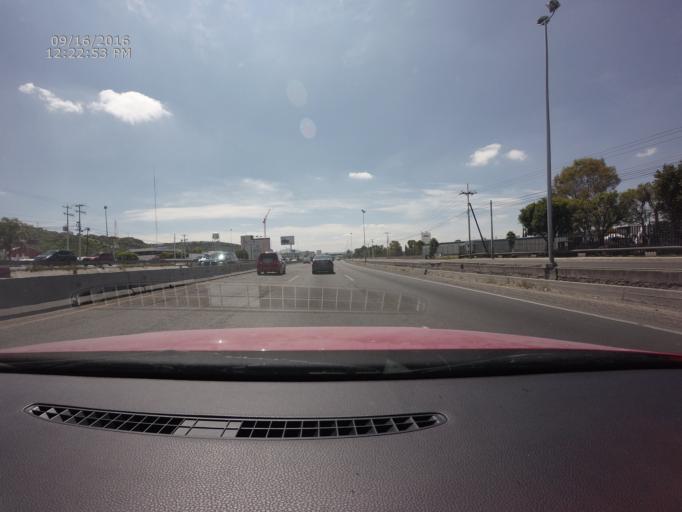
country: MX
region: Queretaro
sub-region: Queretaro
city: Sergio Villasenor
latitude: 20.6336
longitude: -100.4274
